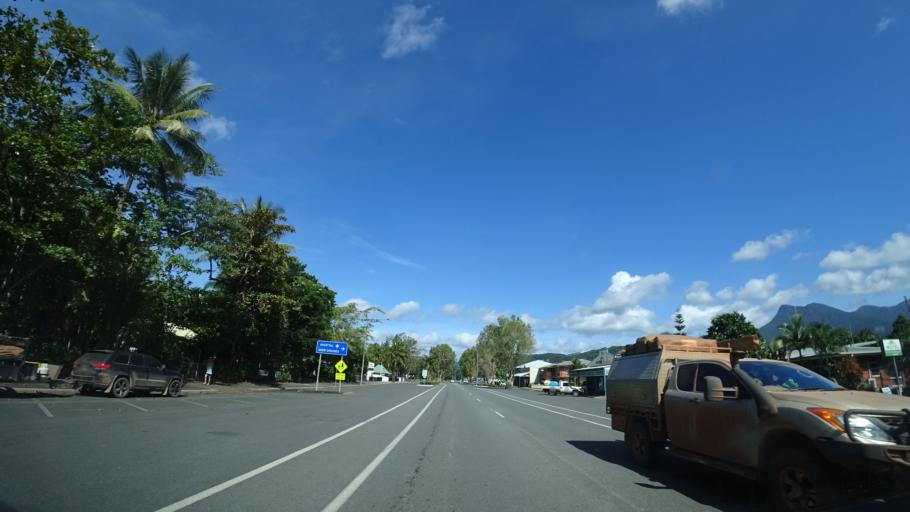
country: AU
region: Queensland
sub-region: Cairns
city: Port Douglas
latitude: -16.4624
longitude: 145.3735
